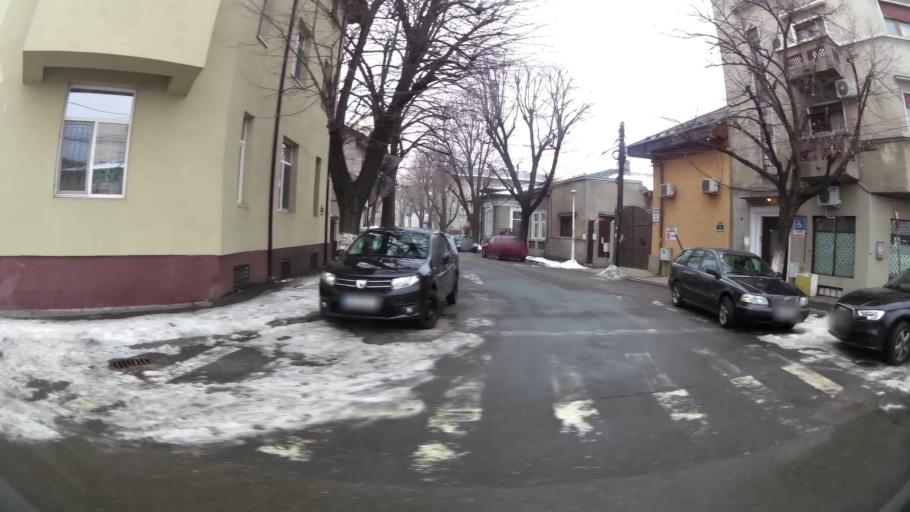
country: RO
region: Bucuresti
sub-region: Municipiul Bucuresti
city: Bucharest
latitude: 44.4423
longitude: 26.1230
